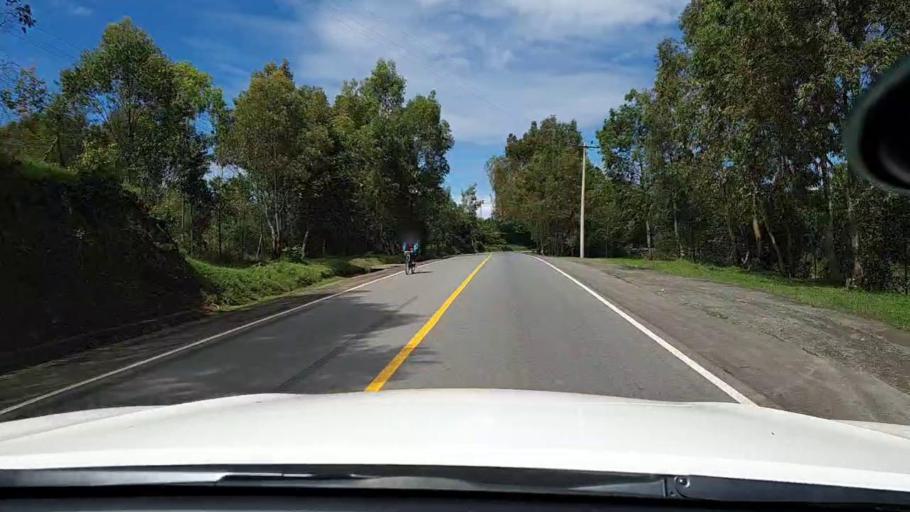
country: RW
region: Kigali
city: Kigali
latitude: -1.8239
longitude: 29.9447
